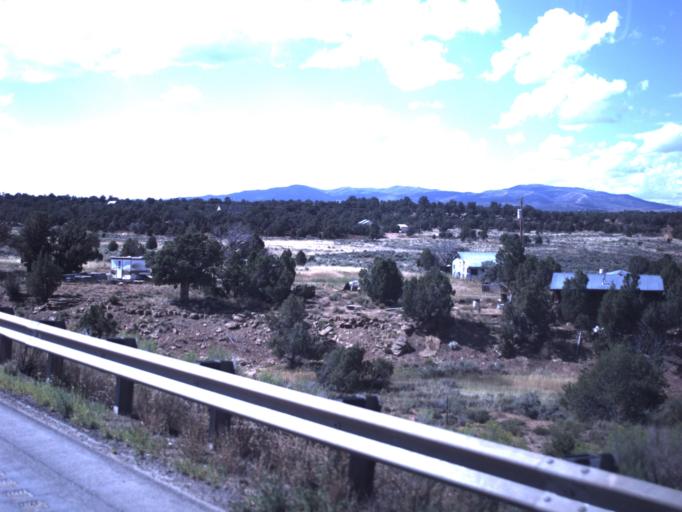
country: US
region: Utah
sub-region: Duchesne County
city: Duchesne
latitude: 40.2071
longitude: -110.8139
